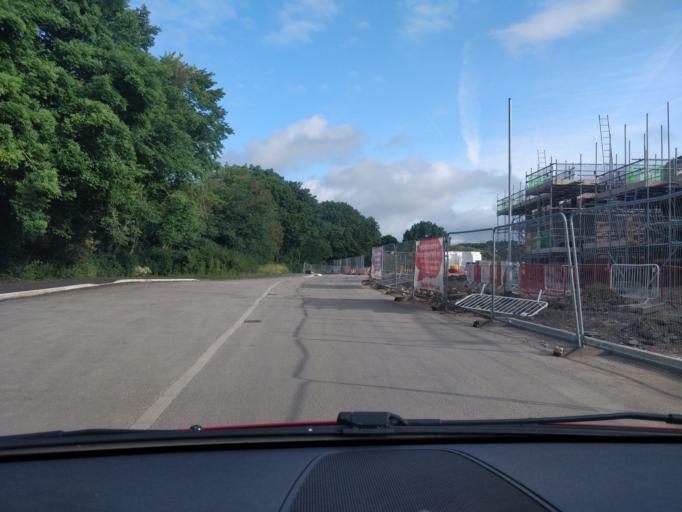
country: GB
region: England
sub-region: Lancashire
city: Banks
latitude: 53.6754
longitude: -2.9160
